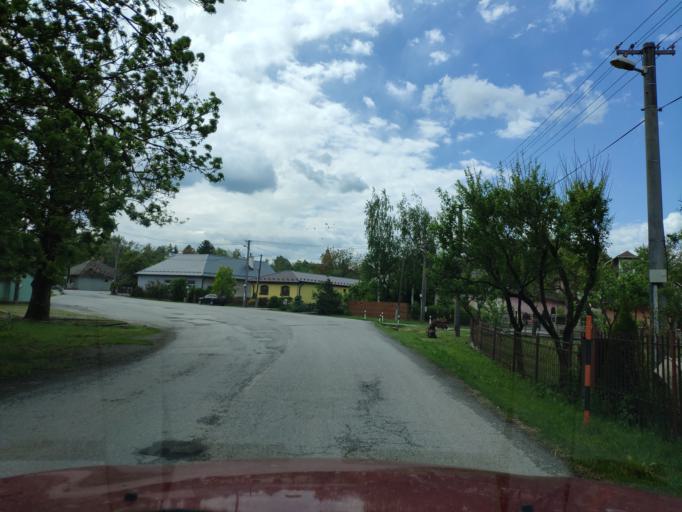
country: SK
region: Kosicky
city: Kosice
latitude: 48.8487
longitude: 21.3178
